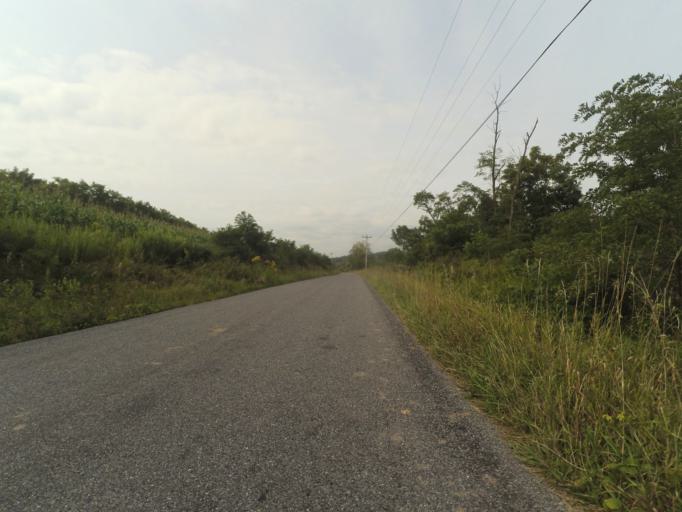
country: US
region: Pennsylvania
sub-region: Huntingdon County
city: Huntingdon
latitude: 40.6000
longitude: -78.0534
